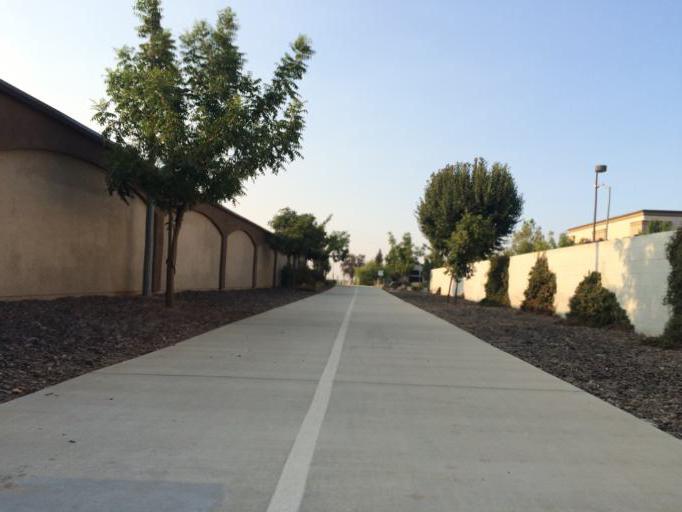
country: US
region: California
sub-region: Fresno County
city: Fresno
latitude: 36.8462
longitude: -119.8106
